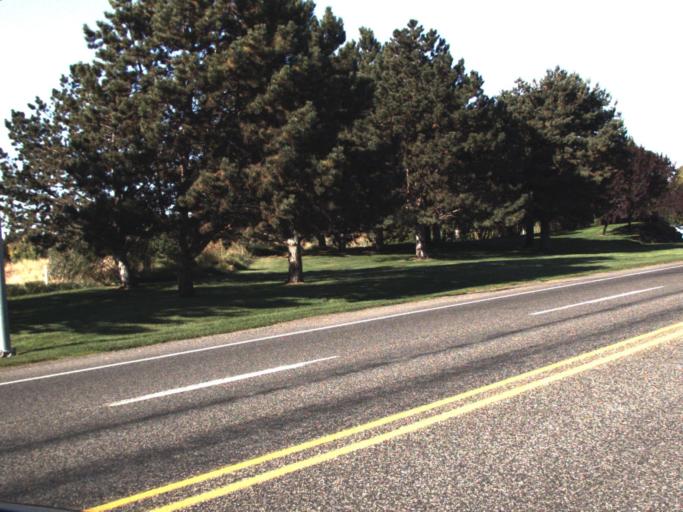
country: US
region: Washington
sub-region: Benton County
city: West Richland
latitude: 46.3253
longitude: -119.3158
